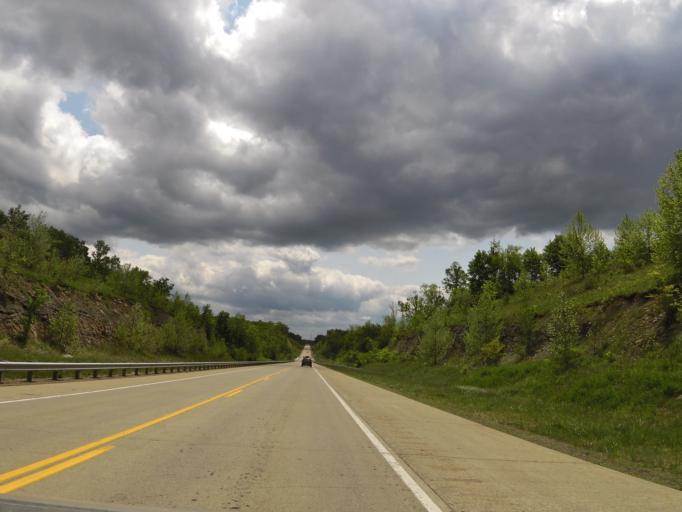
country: US
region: Ohio
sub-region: Meigs County
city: Pomeroy
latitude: 39.1754
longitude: -82.0447
